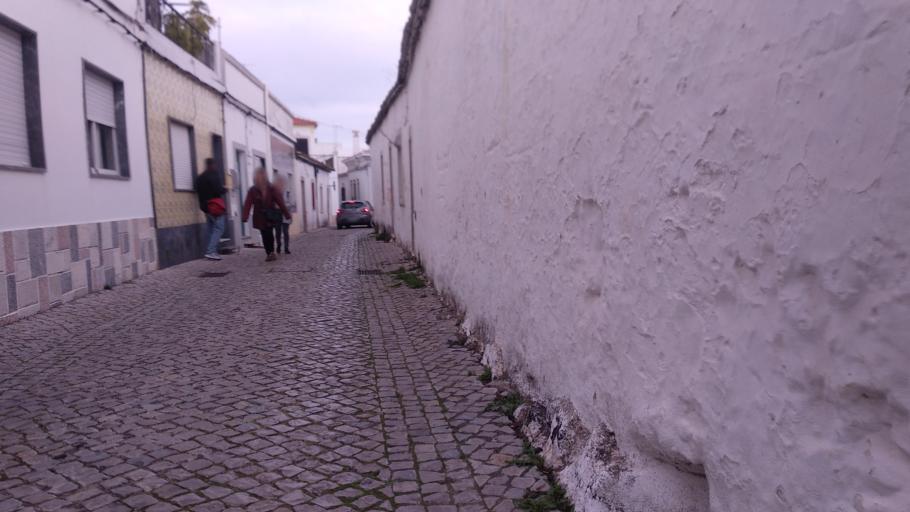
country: PT
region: Faro
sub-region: Sao Bras de Alportel
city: Sao Bras de Alportel
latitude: 37.1513
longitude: -7.8892
